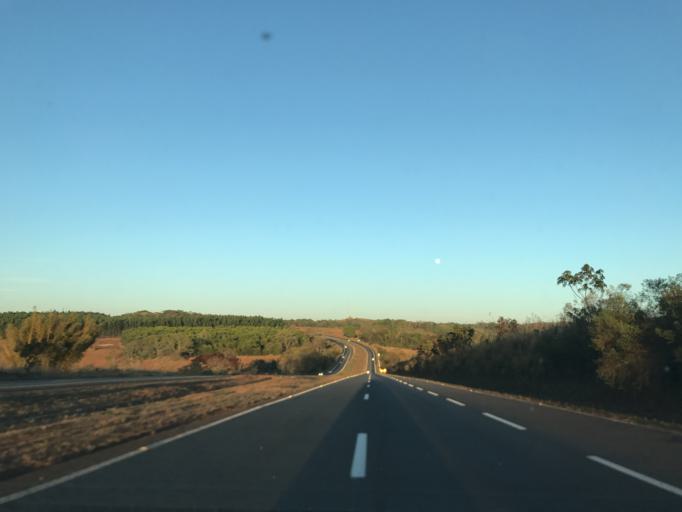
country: BR
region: Goias
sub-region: Abadiania
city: Abadiania
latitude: -16.2765
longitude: -48.7805
